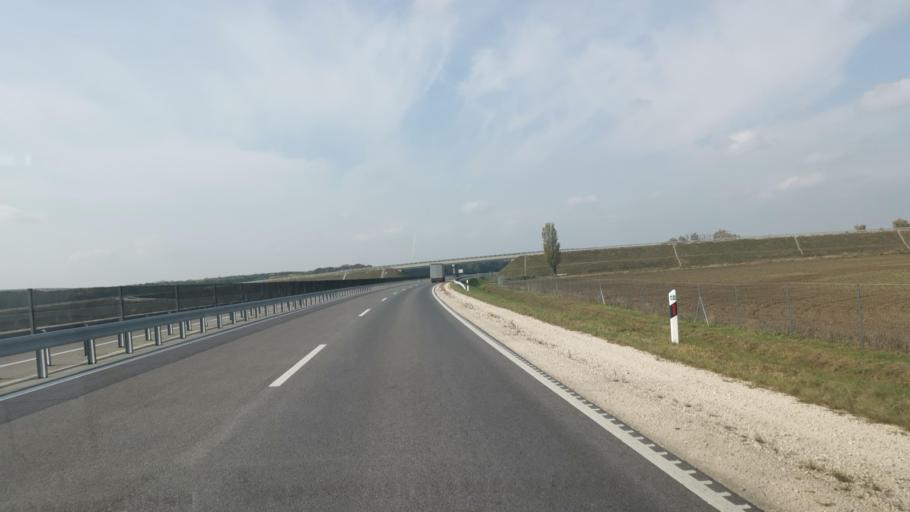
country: HU
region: Gyor-Moson-Sopron
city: Mihalyi
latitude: 47.5616
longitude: 17.0727
